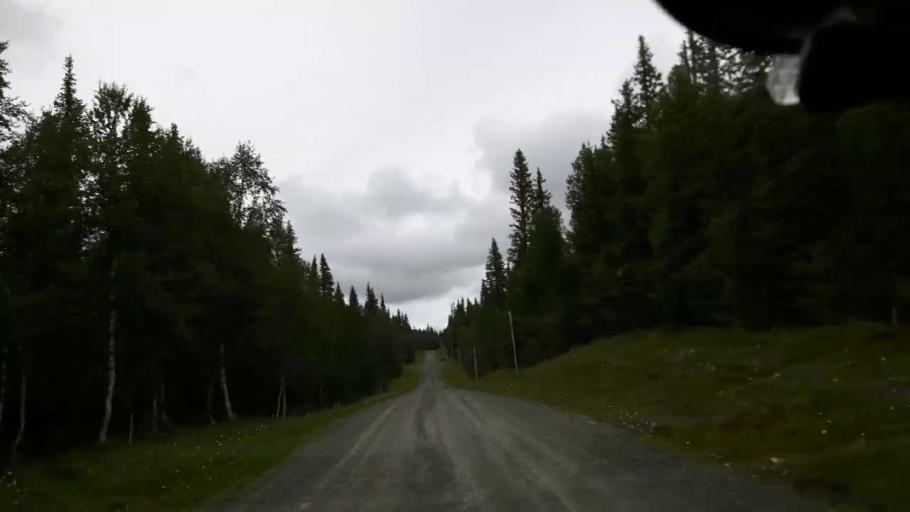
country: SE
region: Jaemtland
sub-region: Krokoms Kommun
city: Valla
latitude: 63.7480
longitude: 13.8354
